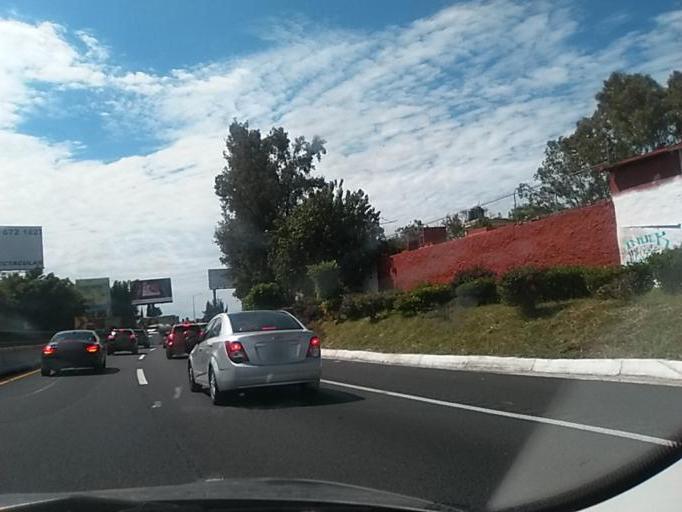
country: MX
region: Morelos
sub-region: Cuernavaca
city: Fraccionamiento Lomas de Ahuatlan
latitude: 18.9770
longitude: -99.2315
